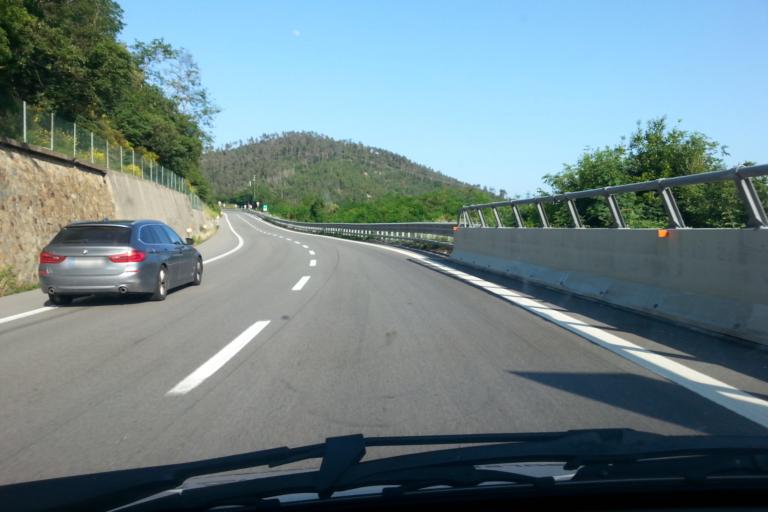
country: IT
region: Liguria
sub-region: Provincia di Savona
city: Quiliano
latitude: 44.2995
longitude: 8.4131
